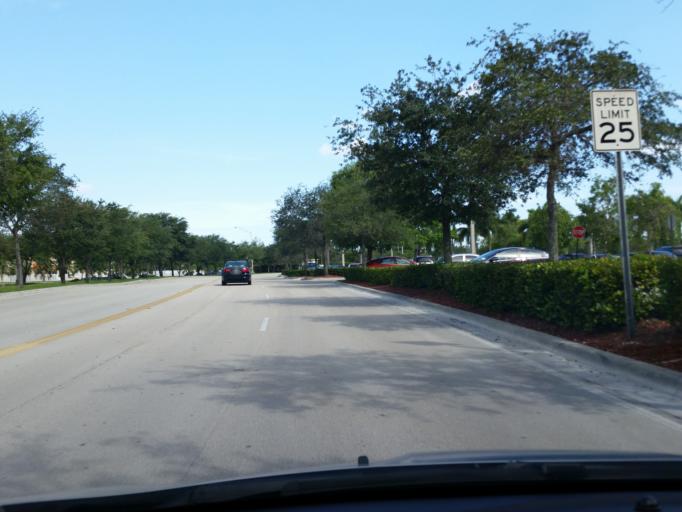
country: US
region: Florida
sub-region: Miami-Dade County
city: Sweetwater
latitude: 25.7892
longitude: -80.3772
